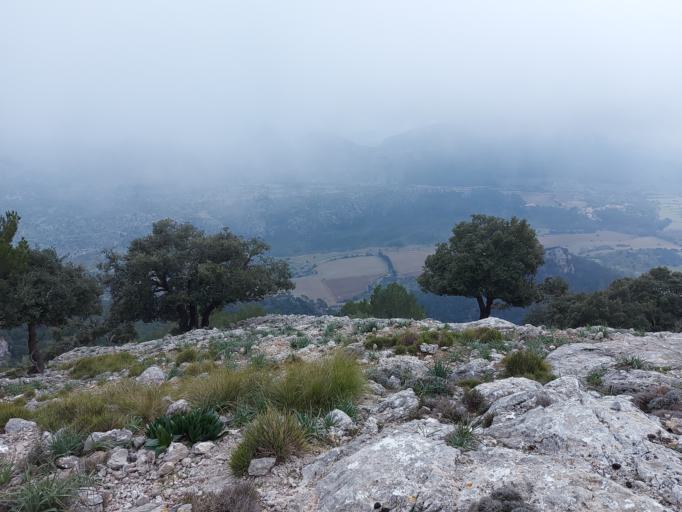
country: ES
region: Balearic Islands
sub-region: Illes Balears
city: Fornalutx
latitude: 39.7516
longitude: 2.7610
